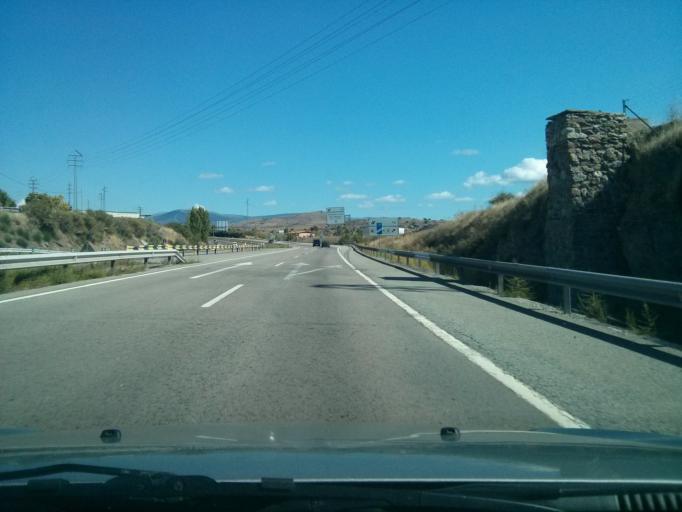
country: ES
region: Madrid
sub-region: Provincia de Madrid
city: Buitrago del Lozoya
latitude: 40.9993
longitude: -3.6398
